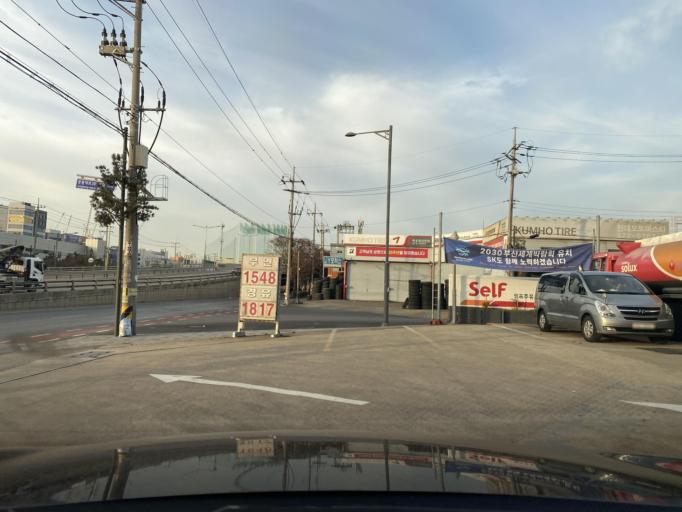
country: KR
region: Incheon
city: Incheon
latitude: 37.5044
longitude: 126.6487
